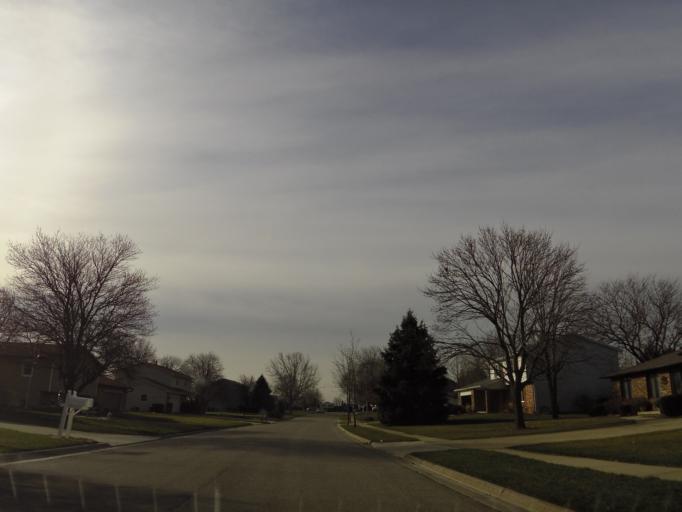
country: US
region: Illinois
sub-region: McLean County
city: Normal
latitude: 40.5088
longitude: -89.0254
